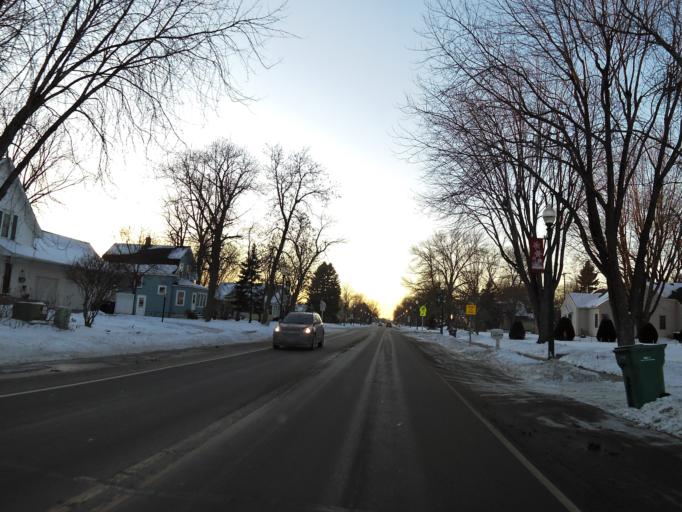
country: US
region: Minnesota
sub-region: Dakota County
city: Rosemount
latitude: 44.7393
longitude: -93.1301
